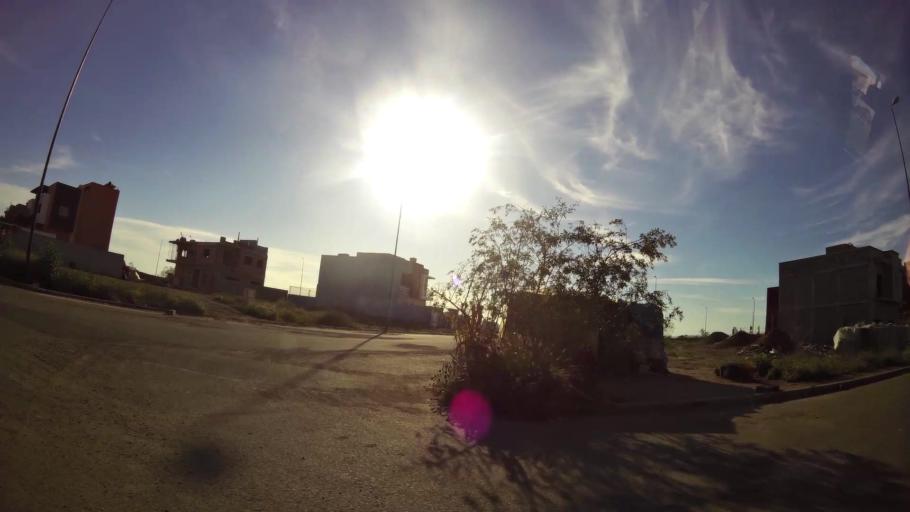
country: MA
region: Marrakech-Tensift-Al Haouz
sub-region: Marrakech
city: Marrakesh
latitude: 31.6712
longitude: -8.0729
